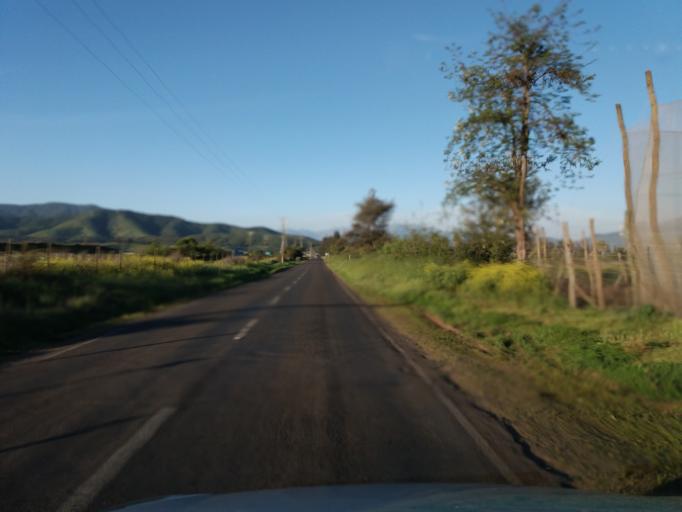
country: CL
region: Valparaiso
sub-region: Provincia de Quillota
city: Quillota
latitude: -32.9107
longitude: -71.3109
